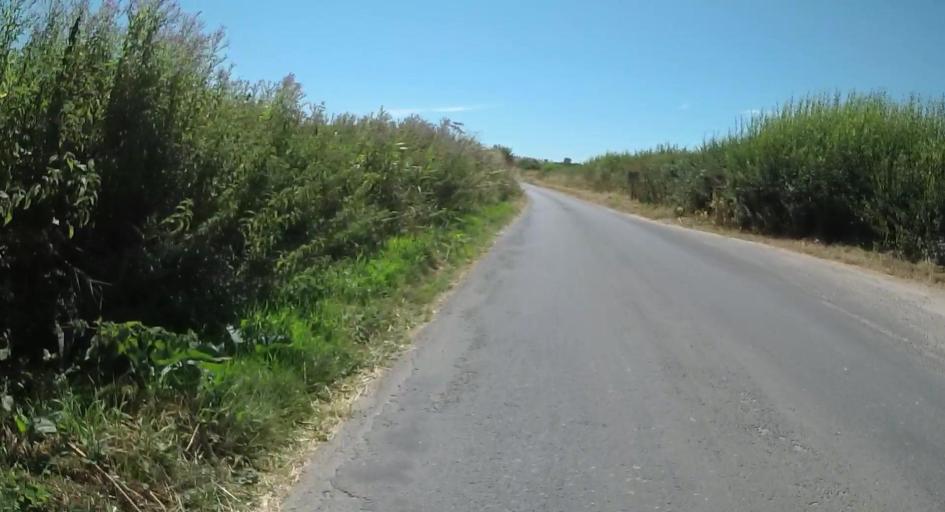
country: GB
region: England
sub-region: Dorset
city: Bovington Camp
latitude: 50.6536
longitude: -2.2846
